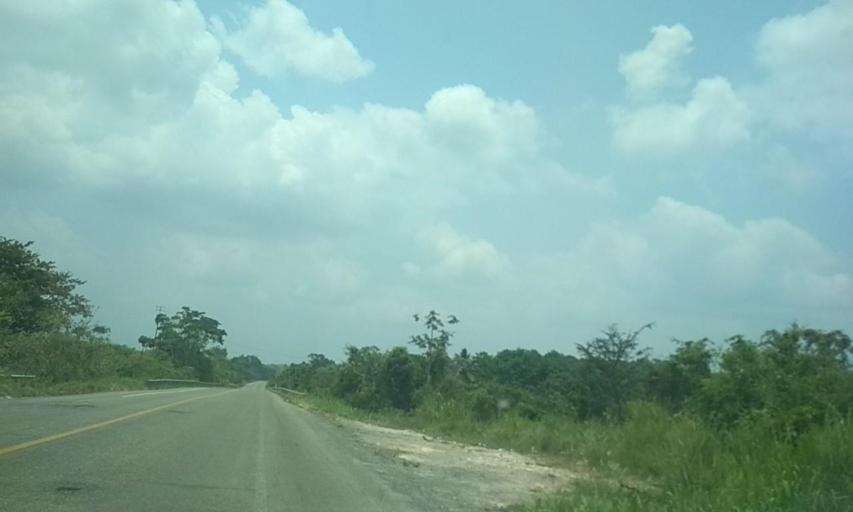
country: MX
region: Tabasco
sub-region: Huimanguillo
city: Francisco Rueda
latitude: 17.6464
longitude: -93.8294
